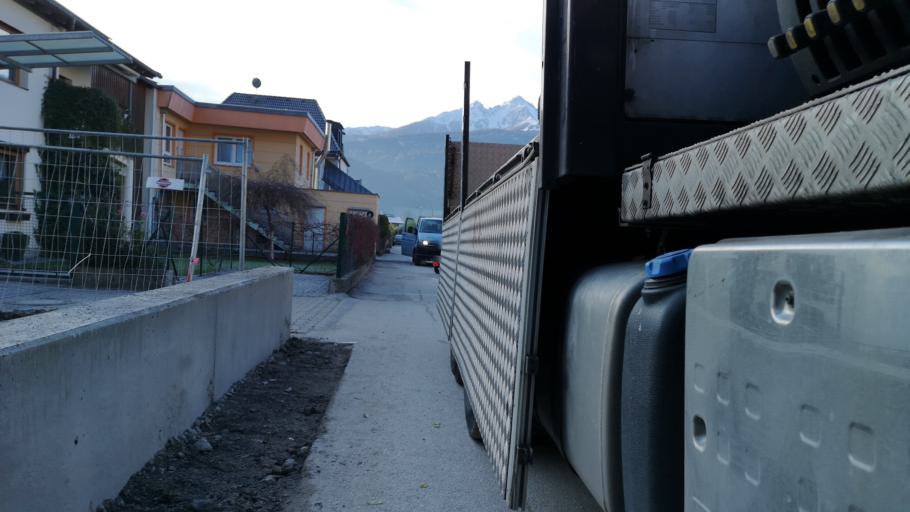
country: AT
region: Tyrol
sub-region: Politischer Bezirk Innsbruck Land
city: Vols
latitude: 47.2664
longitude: 11.3555
